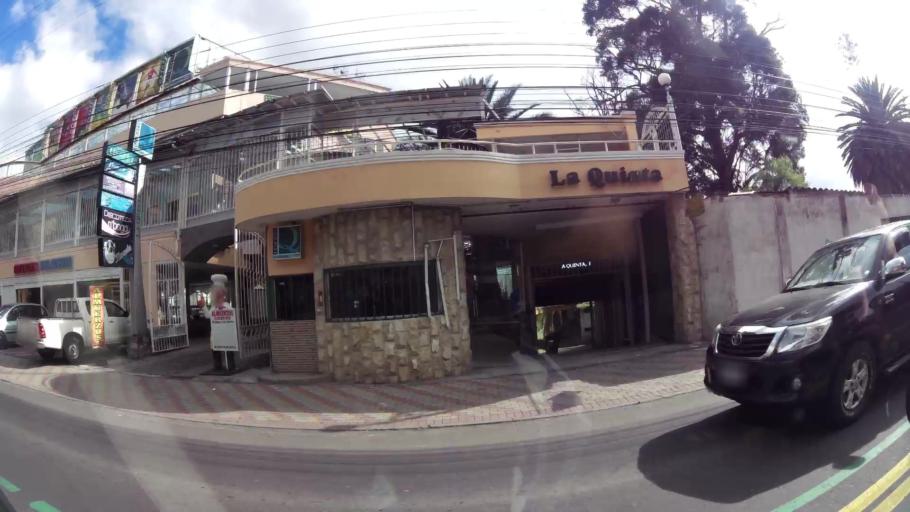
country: EC
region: Pichincha
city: Sangolqui
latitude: -0.3080
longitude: -78.4531
